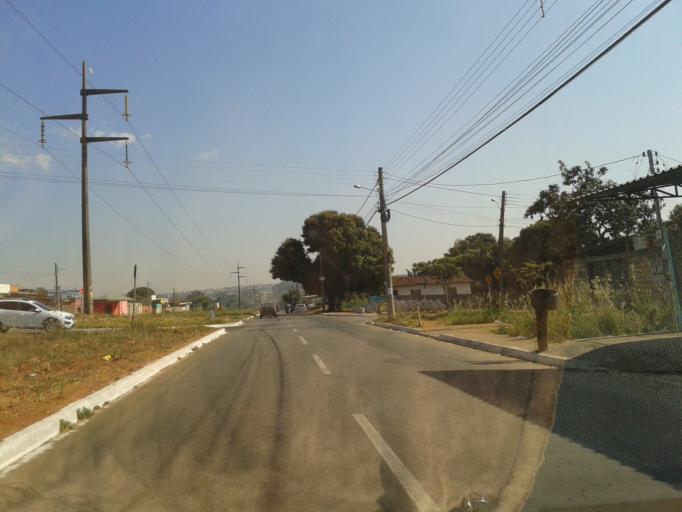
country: BR
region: Goias
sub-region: Aparecida De Goiania
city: Aparecida de Goiania
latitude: -16.7732
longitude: -49.2957
